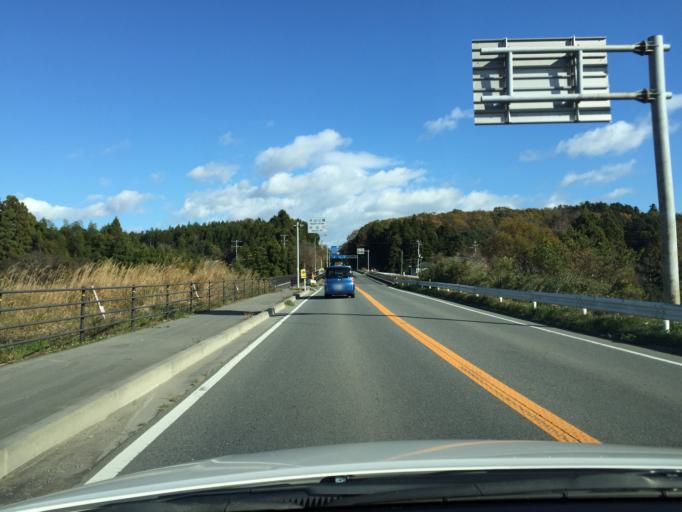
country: JP
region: Fukushima
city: Namie
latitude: 37.2892
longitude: 140.9916
